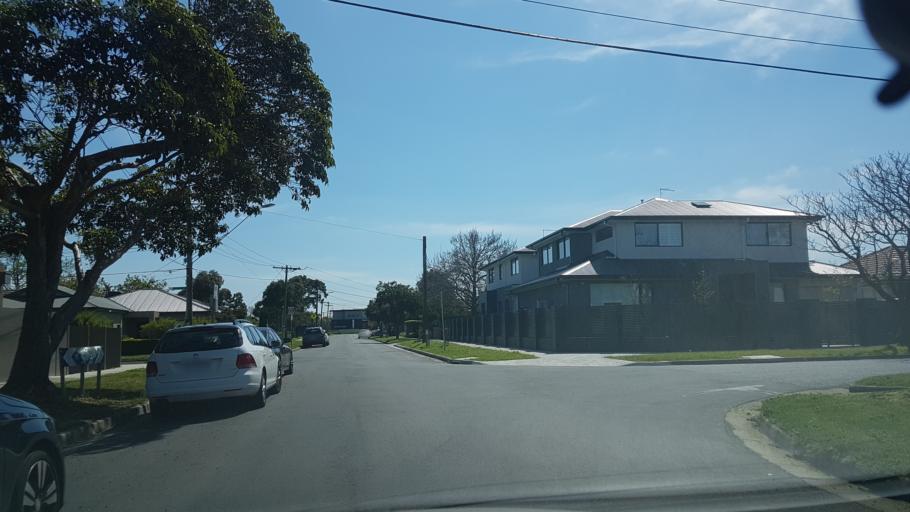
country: AU
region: Victoria
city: Highett
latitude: -37.9343
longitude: 145.0516
